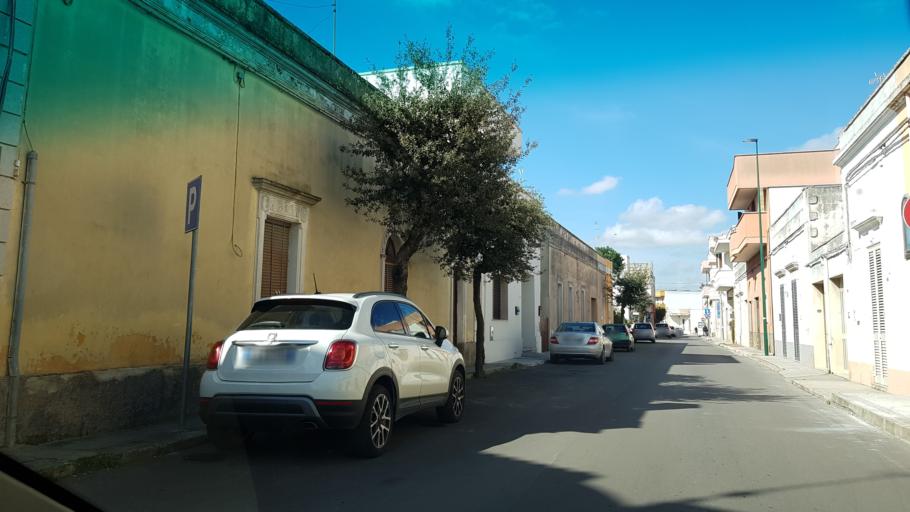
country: IT
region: Apulia
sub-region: Provincia di Lecce
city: Veglie
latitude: 40.3363
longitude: 17.9630
